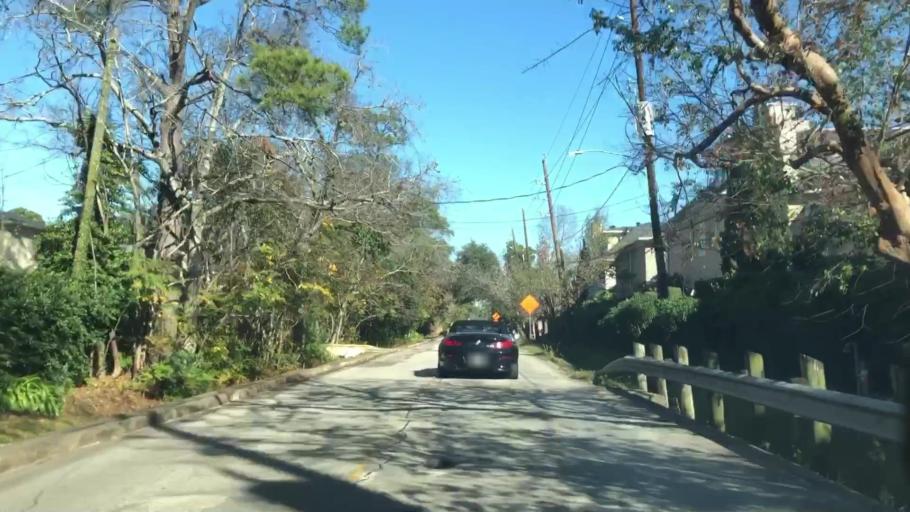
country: US
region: Texas
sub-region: Harris County
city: Hunters Creek Village
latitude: 29.7584
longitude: -95.4676
